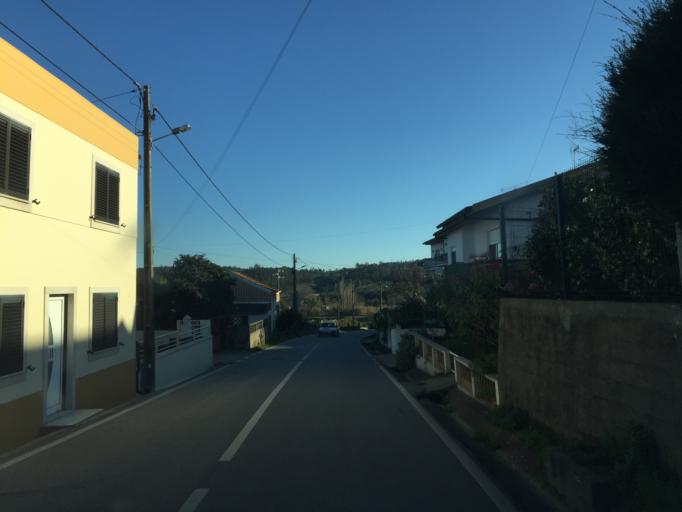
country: PT
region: Coimbra
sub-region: Figueira da Foz
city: Tavarede
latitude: 40.1649
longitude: -8.8187
